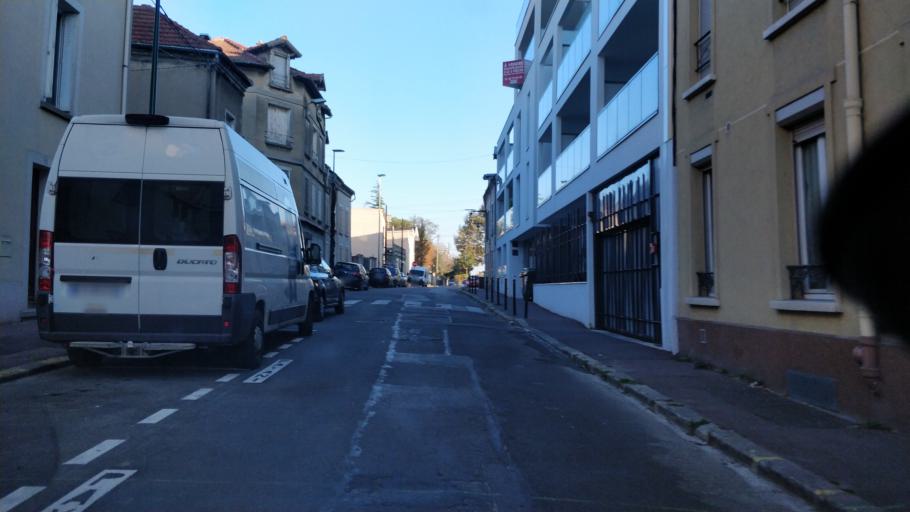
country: FR
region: Ile-de-France
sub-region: Departement de Seine-Saint-Denis
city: Gagny
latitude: 48.8831
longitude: 2.5379
